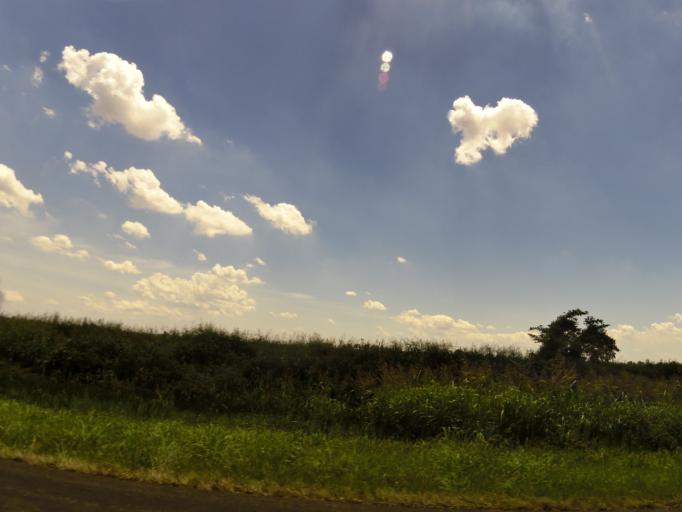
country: US
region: Missouri
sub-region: Pemiscot County
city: Caruthersville
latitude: 36.1882
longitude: -89.7075
